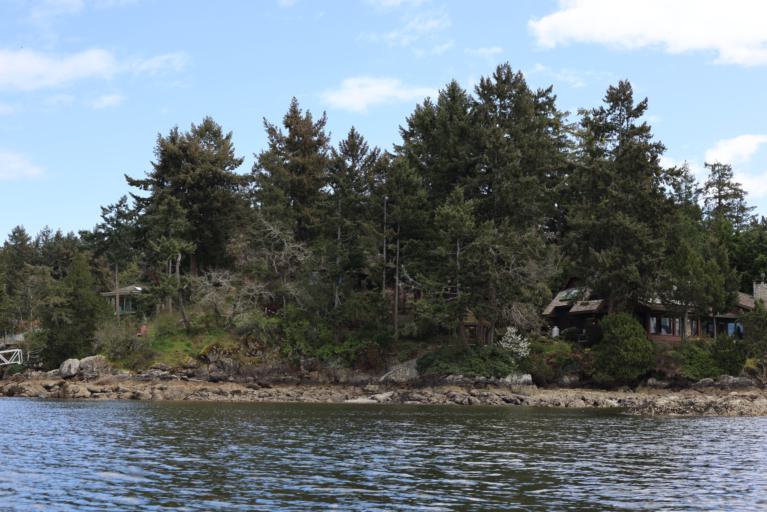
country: CA
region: British Columbia
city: North Saanich
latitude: 48.5989
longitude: -123.4818
